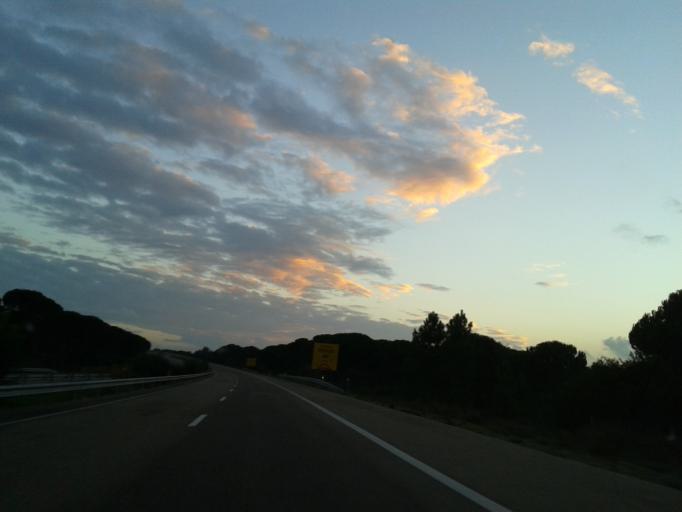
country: PT
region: Evora
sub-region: Vendas Novas
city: Vendas Novas
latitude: 38.6563
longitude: -8.6631
